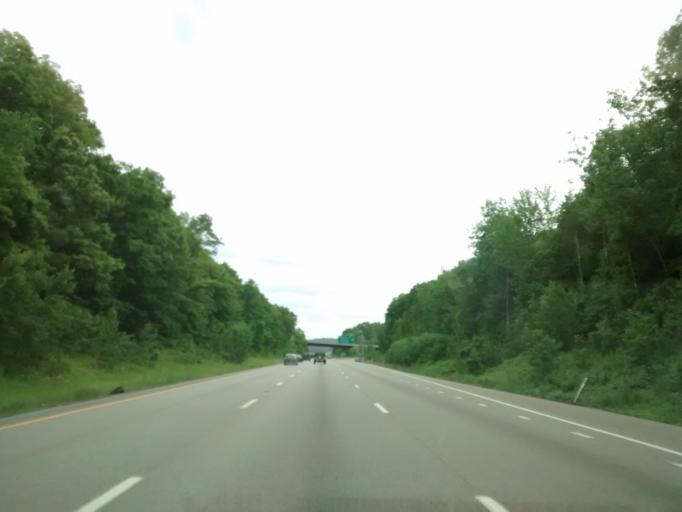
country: US
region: Massachusetts
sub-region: Middlesex County
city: Marlborough
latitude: 42.3263
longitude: -71.5739
